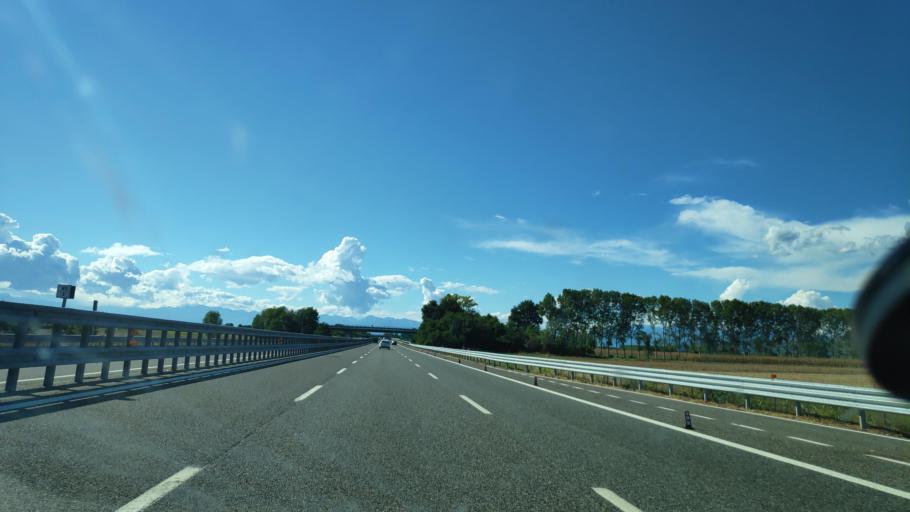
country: IT
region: Piedmont
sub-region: Provincia di Torino
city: Pessione
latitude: 44.9577
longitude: 7.8313
